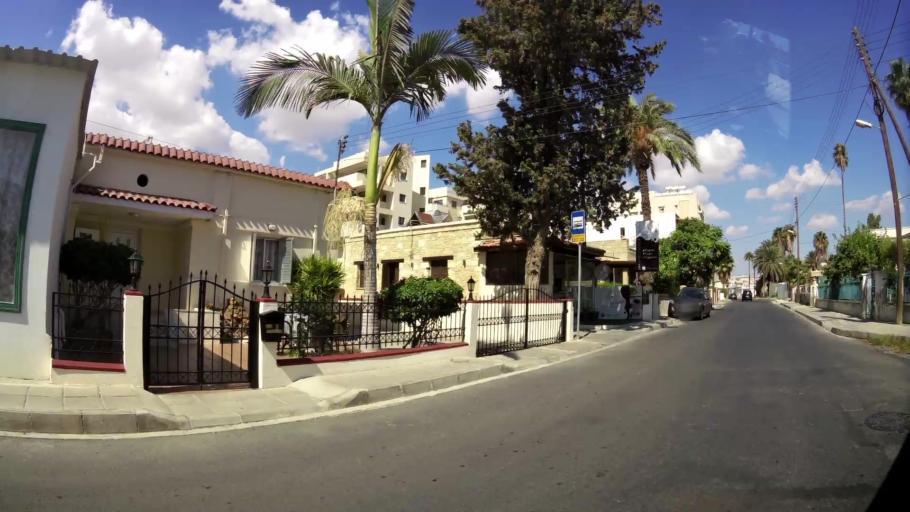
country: CY
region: Larnaka
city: Larnaca
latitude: 34.9077
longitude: 33.6342
